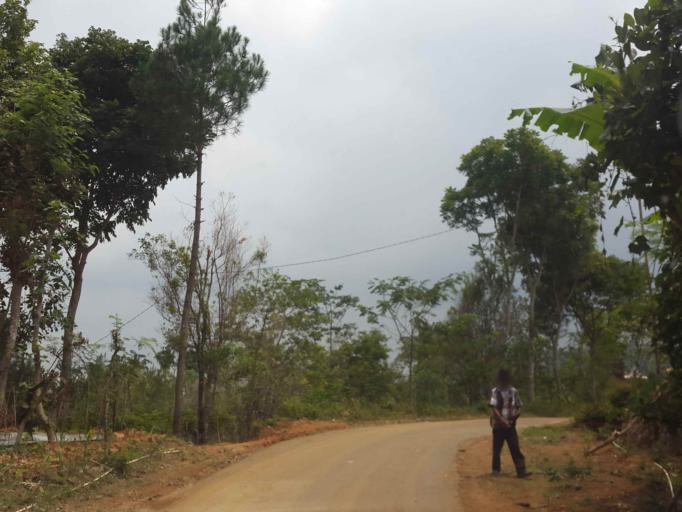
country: ID
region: East Java
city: Krajan Tengah
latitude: -7.9478
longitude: 111.2619
